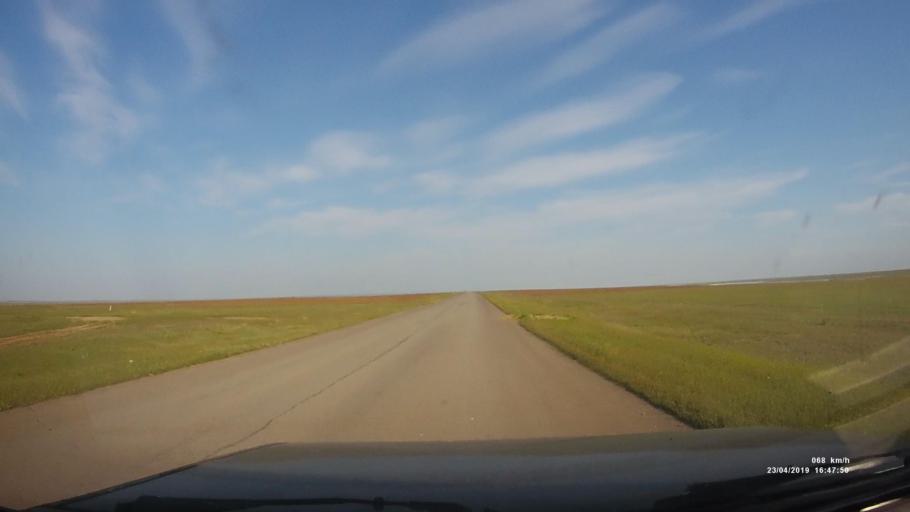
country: RU
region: Kalmykiya
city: Priyutnoye
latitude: 46.3373
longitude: 43.2532
